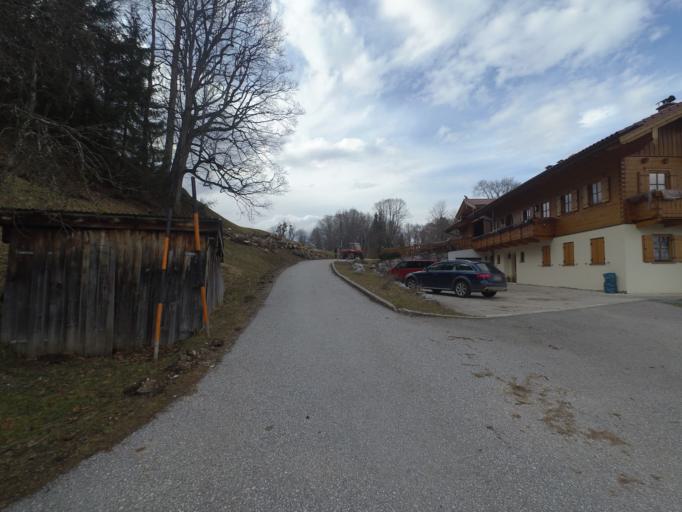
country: AT
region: Salzburg
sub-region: Politischer Bezirk Hallein
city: Hallein
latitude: 47.6600
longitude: 13.0842
